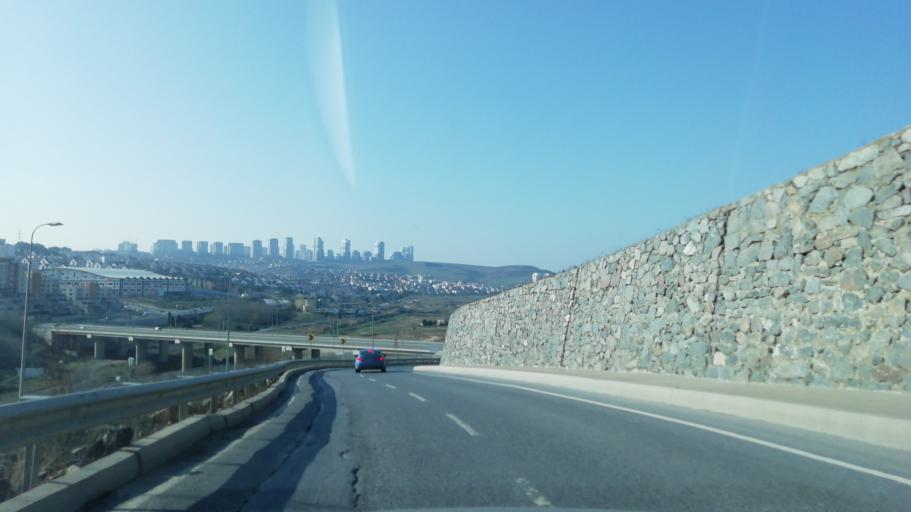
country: TR
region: Istanbul
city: Esenyurt
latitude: 41.0790
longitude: 28.6873
